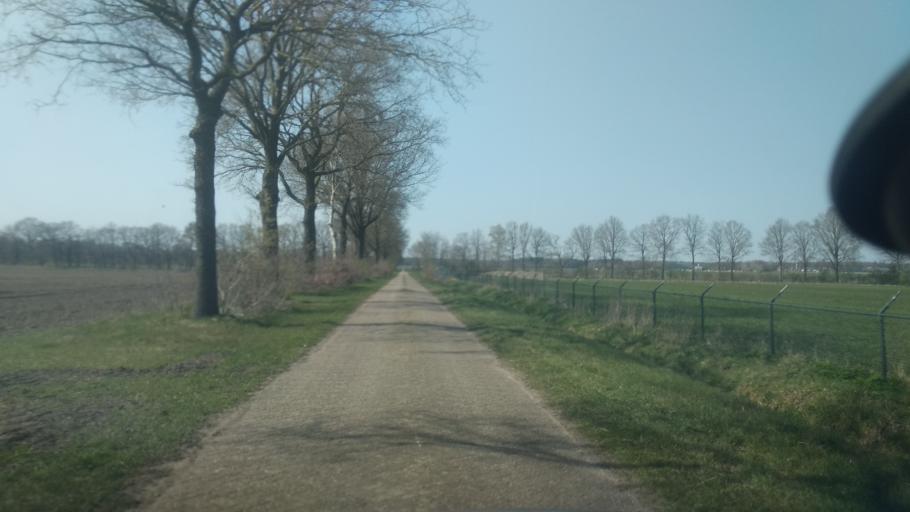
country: NL
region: Drenthe
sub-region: Gemeente Borger-Odoorn
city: Borger
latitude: 52.9125
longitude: 6.7530
